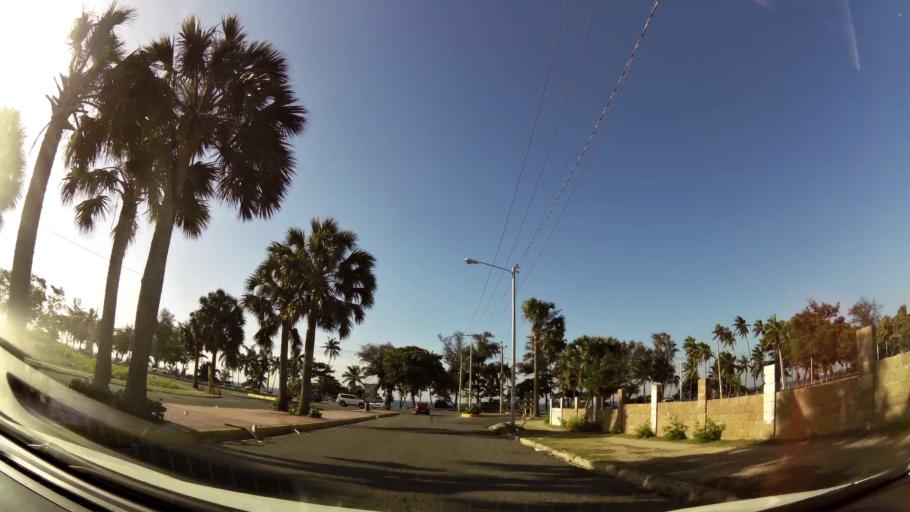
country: DO
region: Santo Domingo
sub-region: Santo Domingo
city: Santo Domingo Este
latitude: 18.4699
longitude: -69.8562
